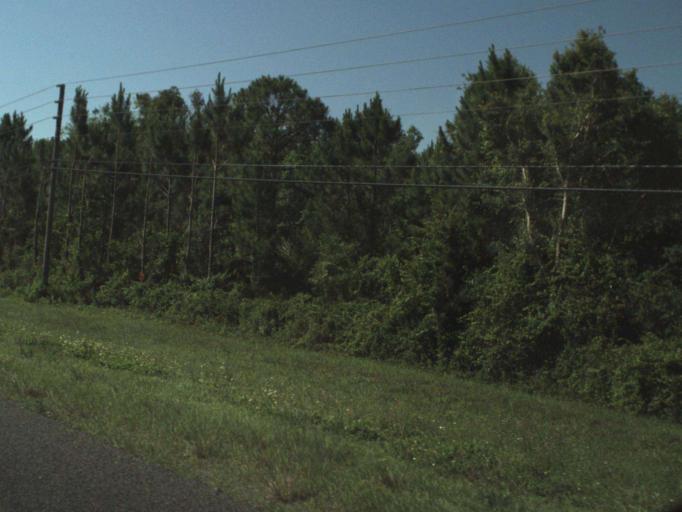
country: US
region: Florida
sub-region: Orange County
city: Christmas
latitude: 28.4330
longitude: -80.9642
